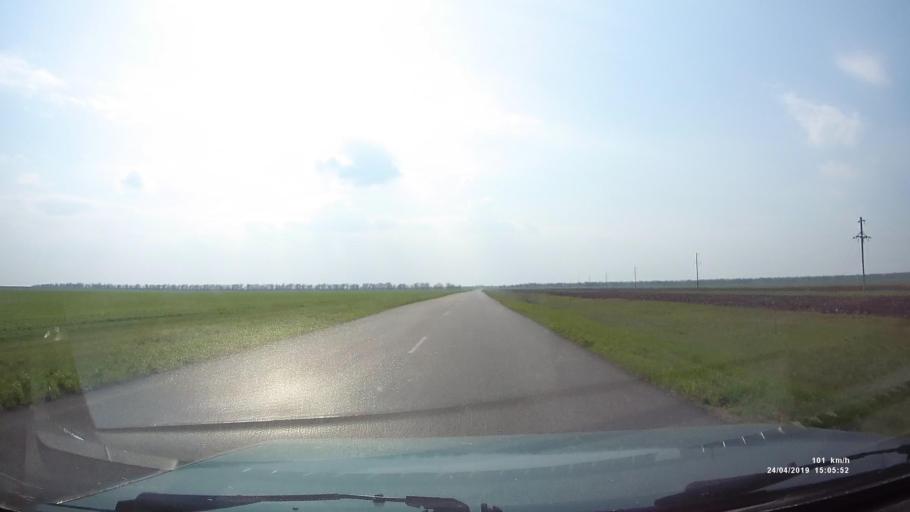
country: RU
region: Rostov
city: Remontnoye
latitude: 46.5594
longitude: 43.4397
